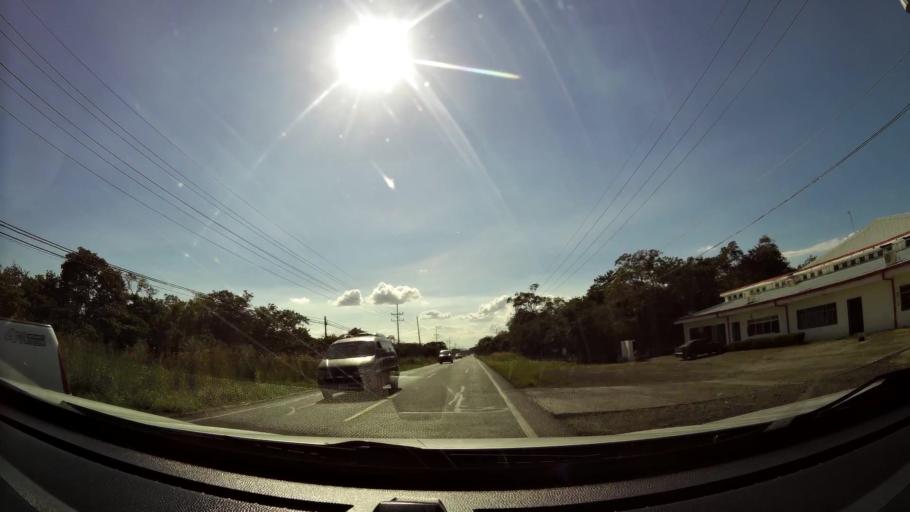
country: CR
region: Guanacaste
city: Liberia
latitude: 10.6025
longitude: -85.5153
